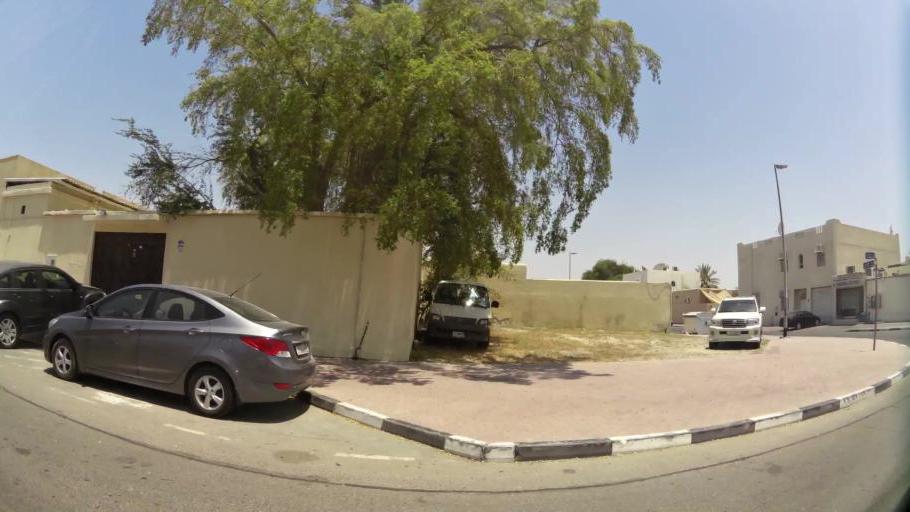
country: AE
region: Ash Shariqah
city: Sharjah
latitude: 25.2904
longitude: 55.3385
